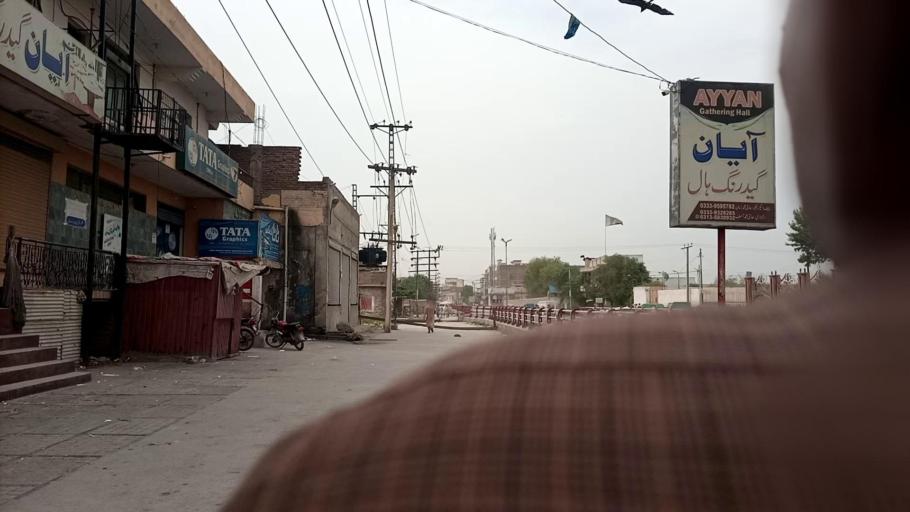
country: PK
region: Khyber Pakhtunkhwa
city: Peshawar
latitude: 34.0176
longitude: 71.5926
